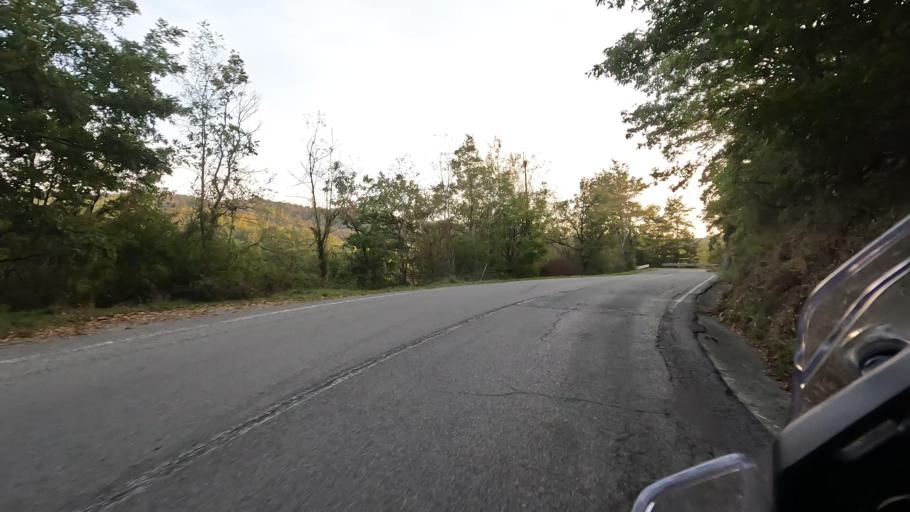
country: IT
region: Liguria
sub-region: Provincia di Savona
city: Mioglia
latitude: 44.5046
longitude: 8.4349
